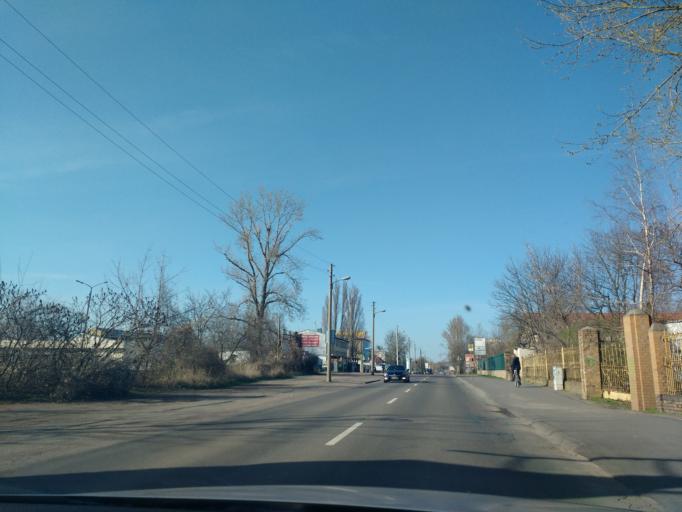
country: DE
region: Saxony-Anhalt
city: Sennewitz
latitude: 51.5237
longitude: 11.9566
